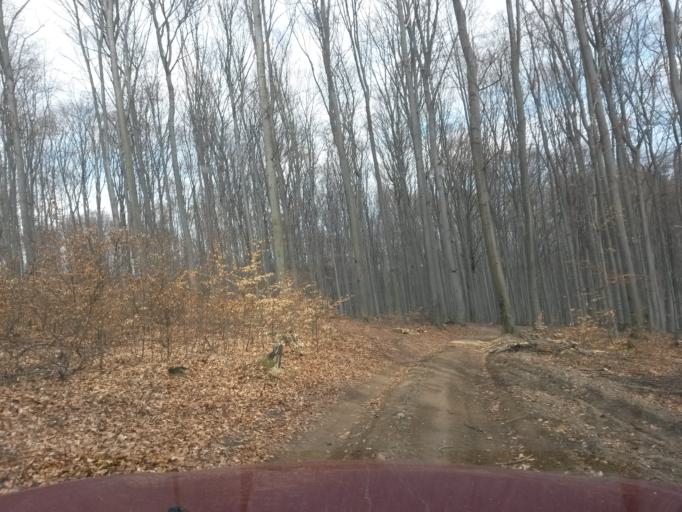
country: SK
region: Presovsky
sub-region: Okres Presov
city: Presov
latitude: 48.9324
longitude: 21.1399
